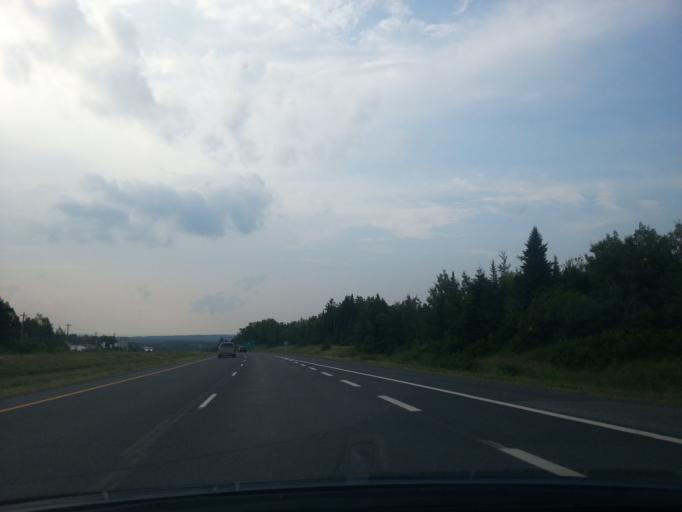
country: CA
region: New Brunswick
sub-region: Madawaska County
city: Saint-Leonard
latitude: 47.1758
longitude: -67.9194
